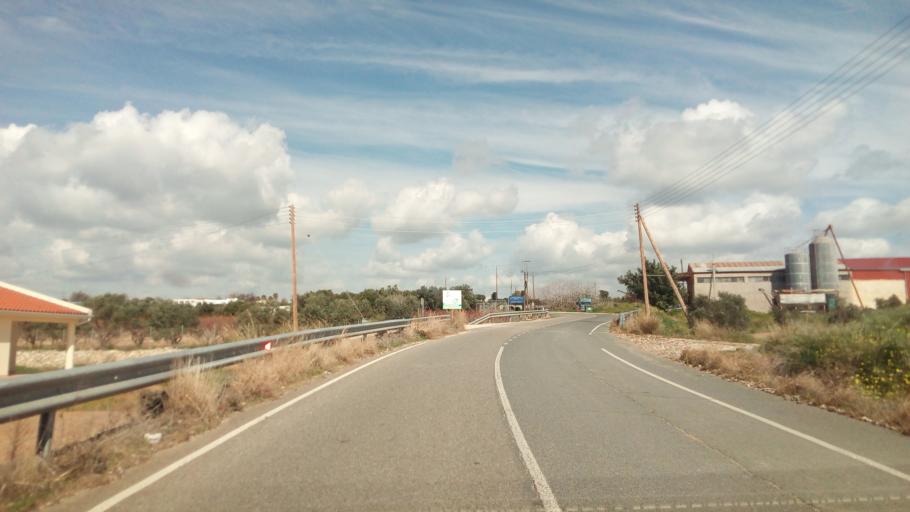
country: CY
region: Pafos
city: Mesogi
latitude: 34.7270
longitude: 32.5308
